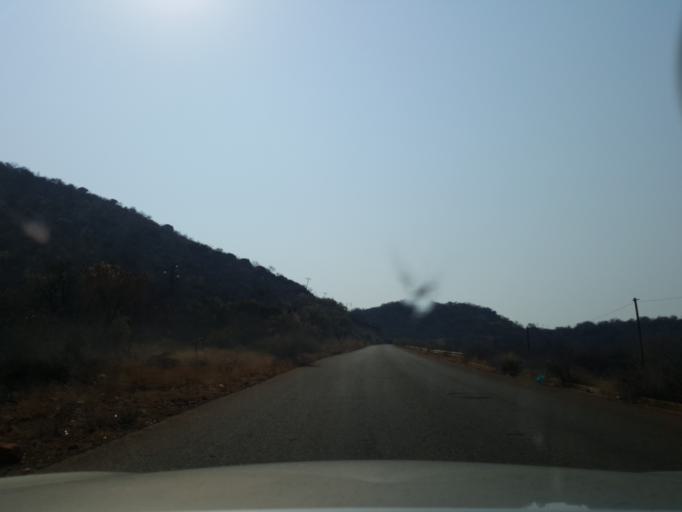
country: BW
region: South East
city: Lobatse
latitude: -25.2846
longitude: 25.8669
